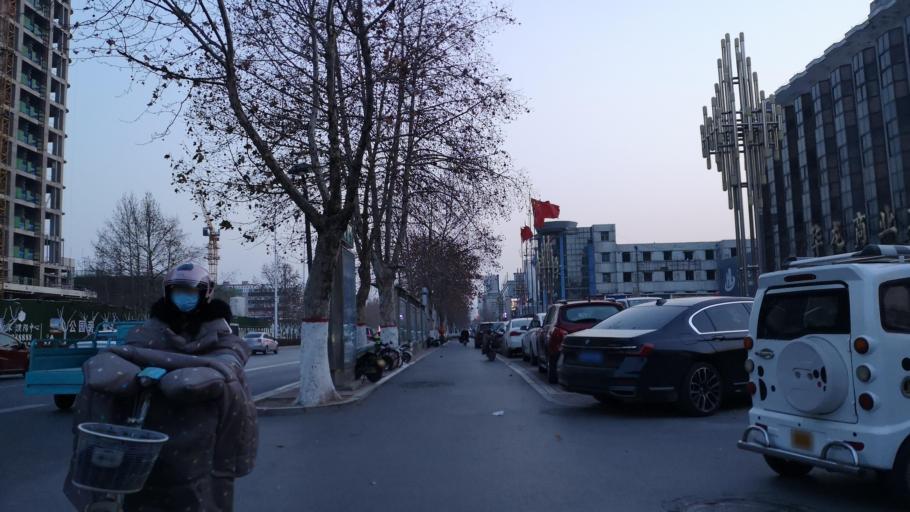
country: CN
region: Henan Sheng
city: Zhongyuanlu
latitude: 35.7756
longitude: 115.0704
